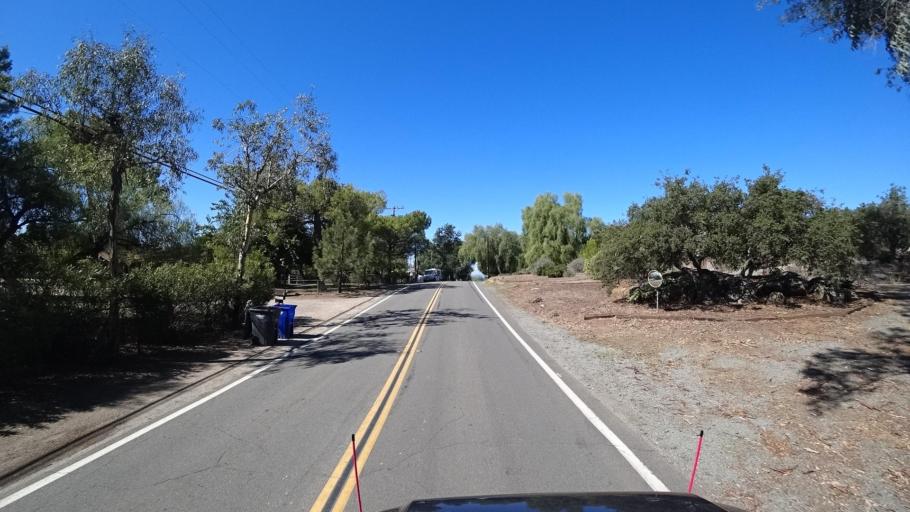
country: US
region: California
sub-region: San Diego County
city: Alpine
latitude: 32.8488
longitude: -116.7556
